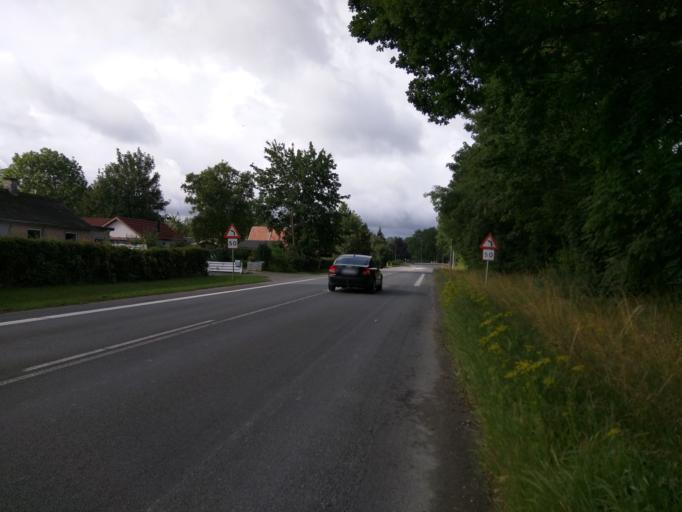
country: DK
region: Zealand
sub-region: Kalundborg Kommune
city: Svebolle
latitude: 55.6774
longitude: 11.2973
